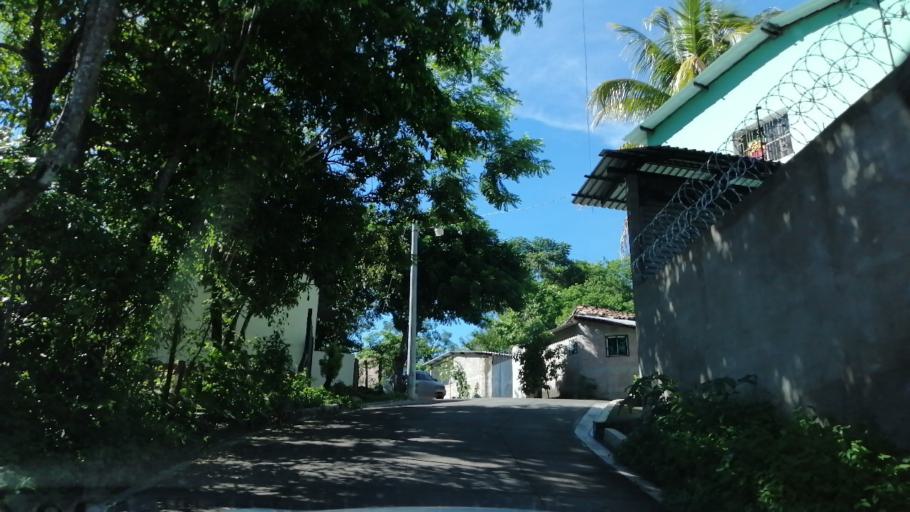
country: SV
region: Morazan
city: Corinto
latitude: 13.8059
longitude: -87.9713
